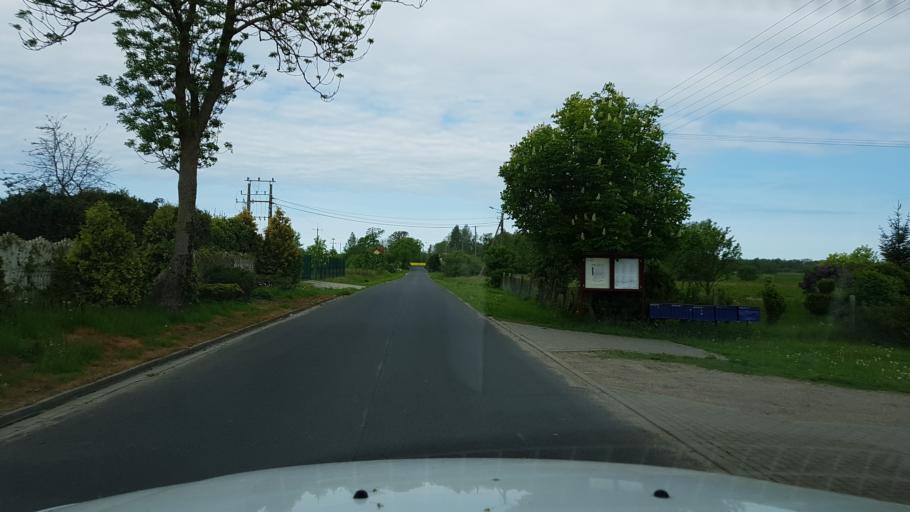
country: PL
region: West Pomeranian Voivodeship
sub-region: Powiat kolobrzeski
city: Ustronie Morskie
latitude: 54.2195
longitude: 15.8104
